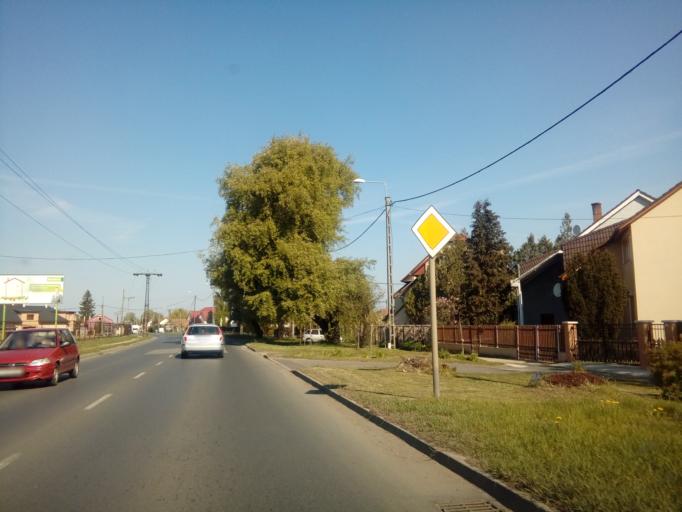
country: HU
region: Szabolcs-Szatmar-Bereg
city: Nyiregyhaza
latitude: 47.9341
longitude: 21.7559
